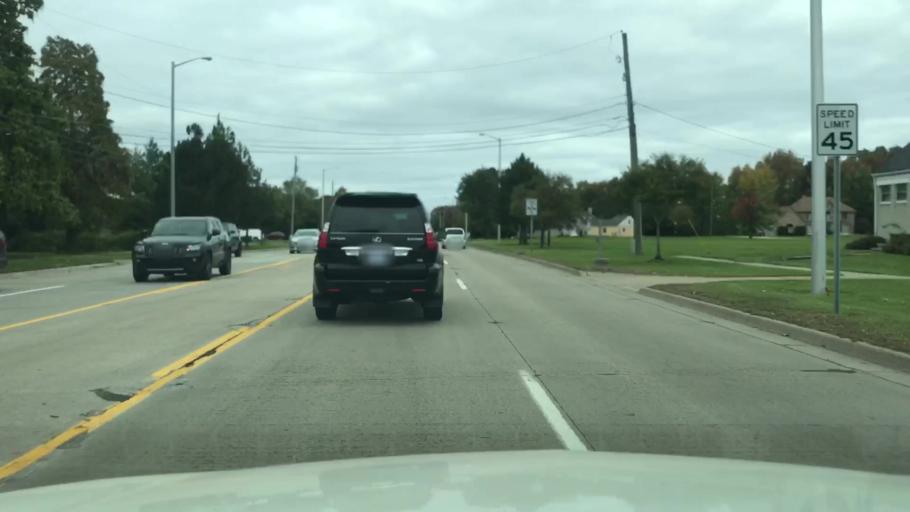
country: US
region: Michigan
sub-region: Macomb County
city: Sterling Heights
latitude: 42.5799
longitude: -83.0703
